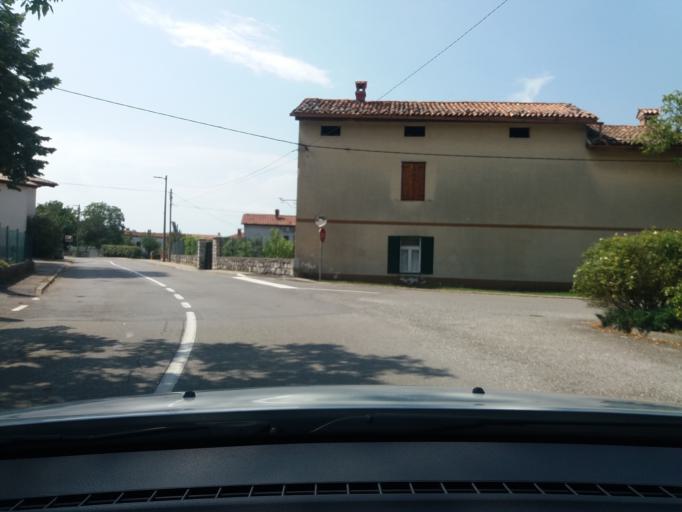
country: IT
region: Friuli Venezia Giulia
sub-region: Provincia di Gorizia
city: Doberdo del Lago
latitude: 45.8532
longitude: 13.5823
